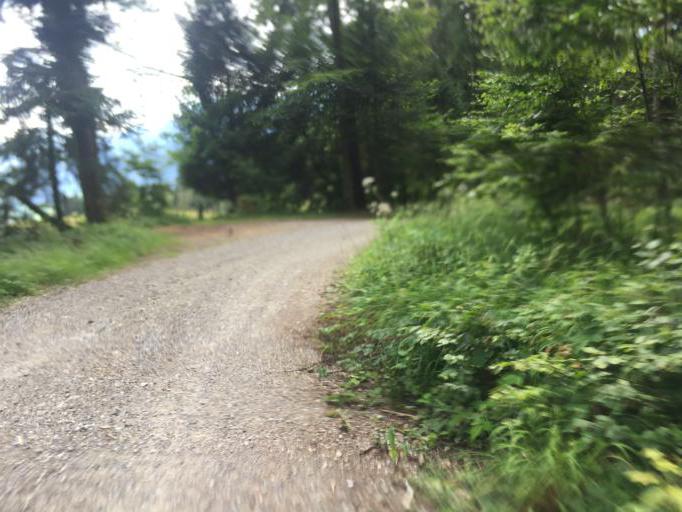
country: CH
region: Bern
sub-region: Thun District
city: Wattenwil
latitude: 46.7538
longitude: 7.4833
